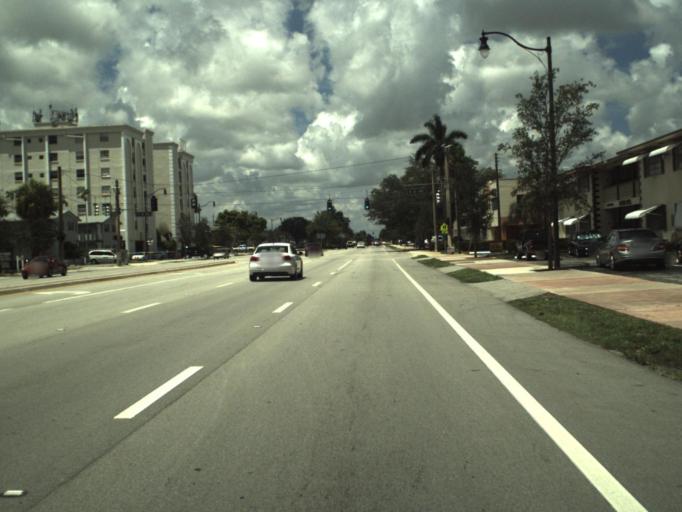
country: US
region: Florida
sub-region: Broward County
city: Carver Ranches
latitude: 26.0104
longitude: -80.1948
